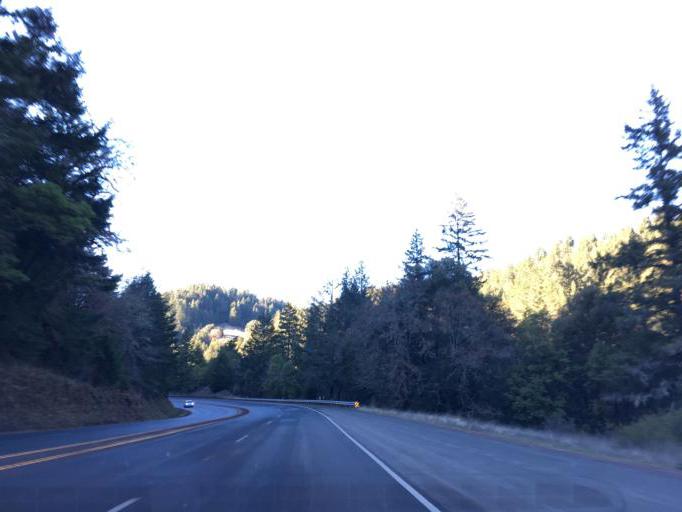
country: US
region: California
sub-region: Mendocino County
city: Laytonville
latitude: 39.8283
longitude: -123.5978
